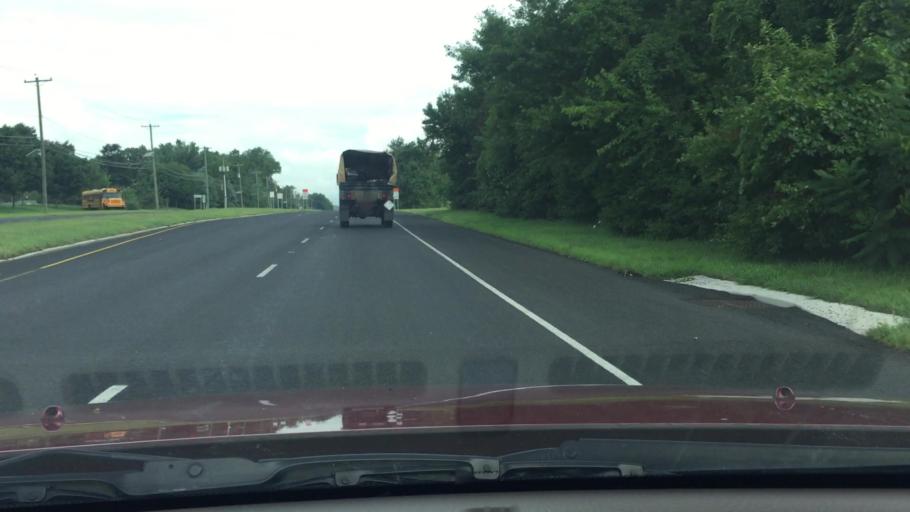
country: US
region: New Jersey
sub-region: Burlington County
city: Bordentown
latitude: 40.0923
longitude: -74.6803
